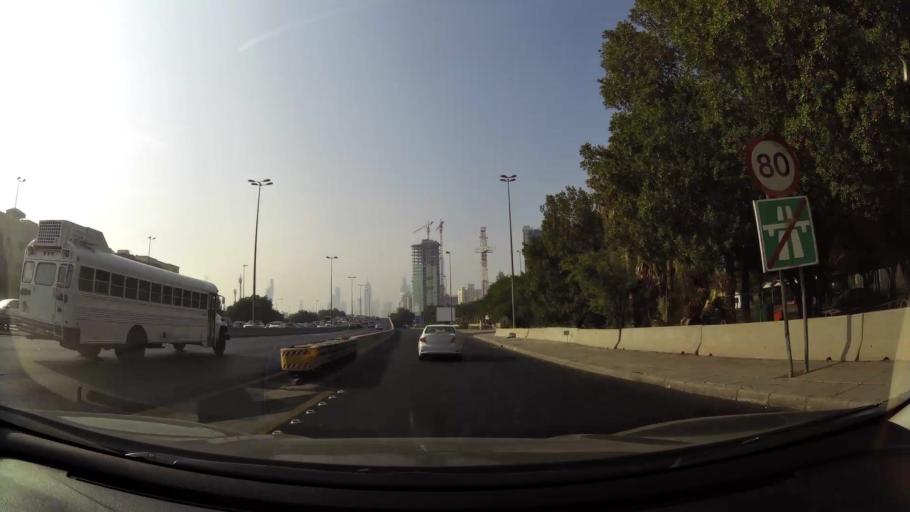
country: KW
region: Al Asimah
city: Ad Dasmah
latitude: 29.3642
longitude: 48.0139
